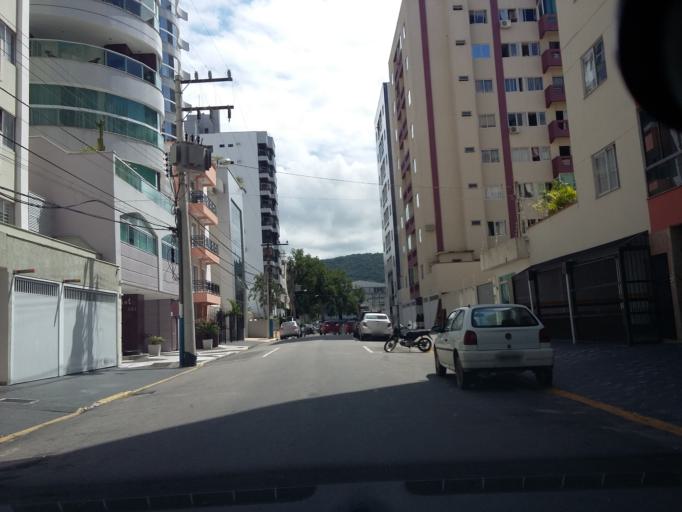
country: BR
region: Santa Catarina
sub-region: Balneario Camboriu
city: Balneario Camboriu
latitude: -26.9787
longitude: -48.6383
